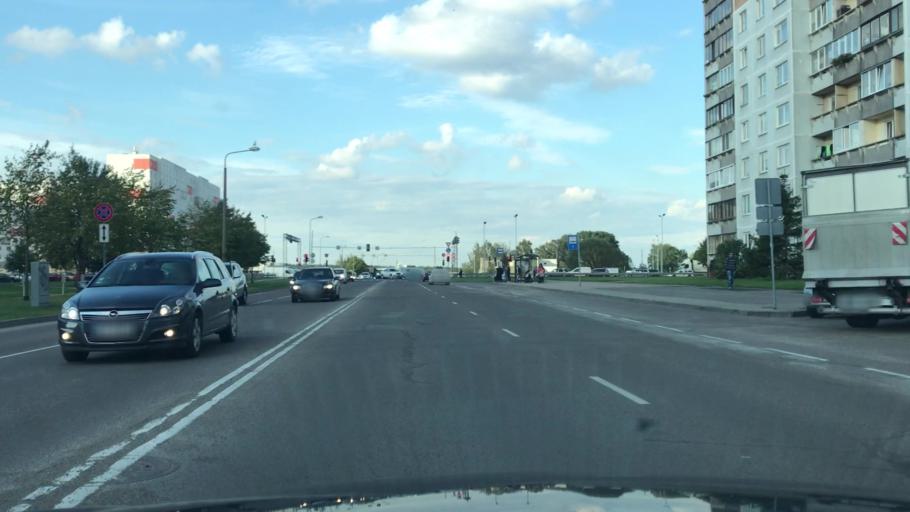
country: LV
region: Stopini
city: Ulbroka
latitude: 56.9437
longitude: 24.2170
